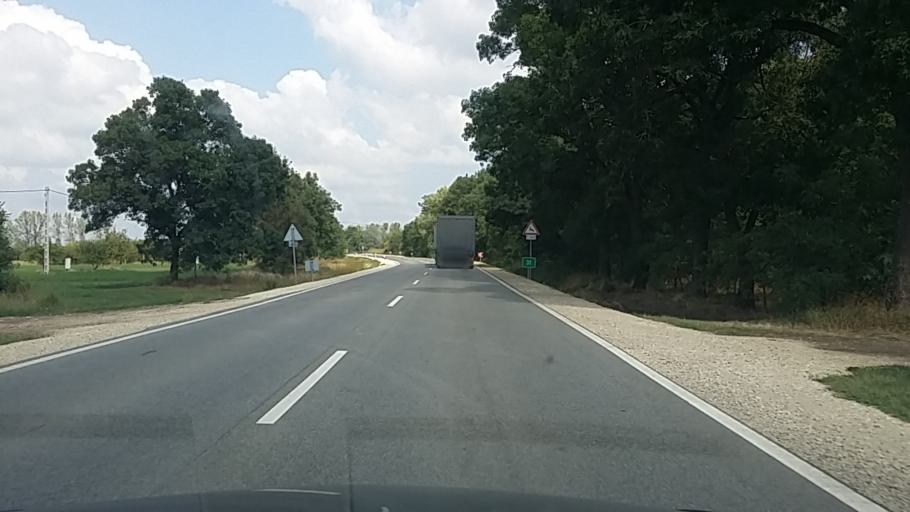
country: HU
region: Csongrad
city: Szentes
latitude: 46.6015
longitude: 20.2931
